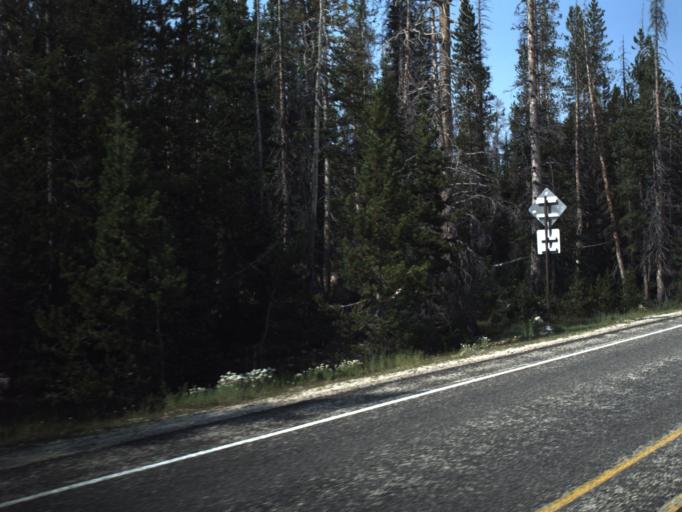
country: US
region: Utah
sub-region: Summit County
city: Kamas
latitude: 40.6783
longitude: -110.9408
